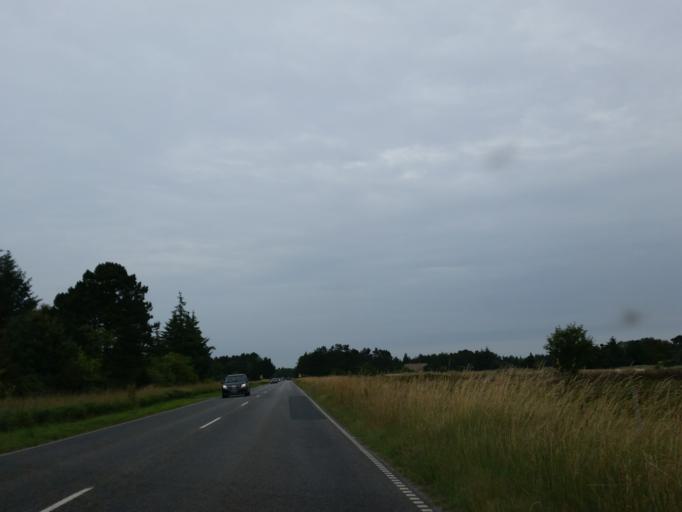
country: DE
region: Schleswig-Holstein
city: List
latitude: 55.1019
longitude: 8.5424
